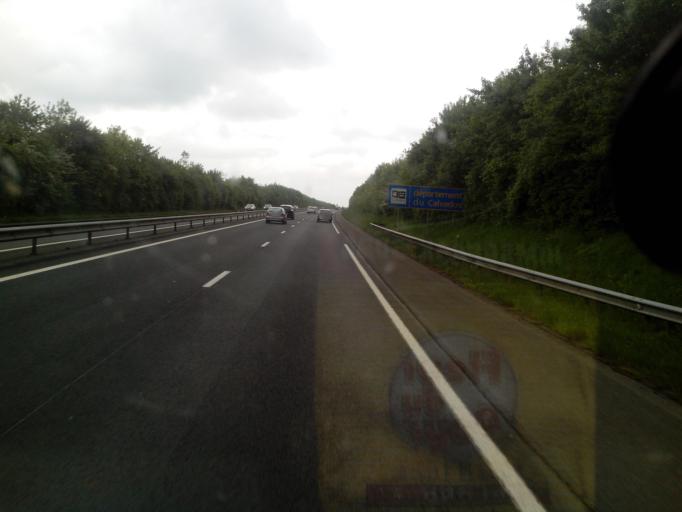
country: FR
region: Lower Normandy
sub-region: Departement du Calvados
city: Saint-Martin-des-Besaces
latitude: 49.0019
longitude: -0.9086
